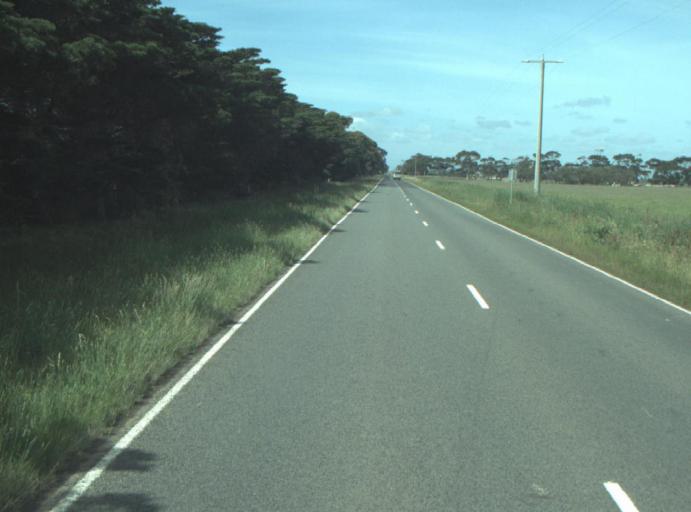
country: AU
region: Victoria
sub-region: Greater Geelong
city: Lara
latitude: -38.0491
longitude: 144.4288
